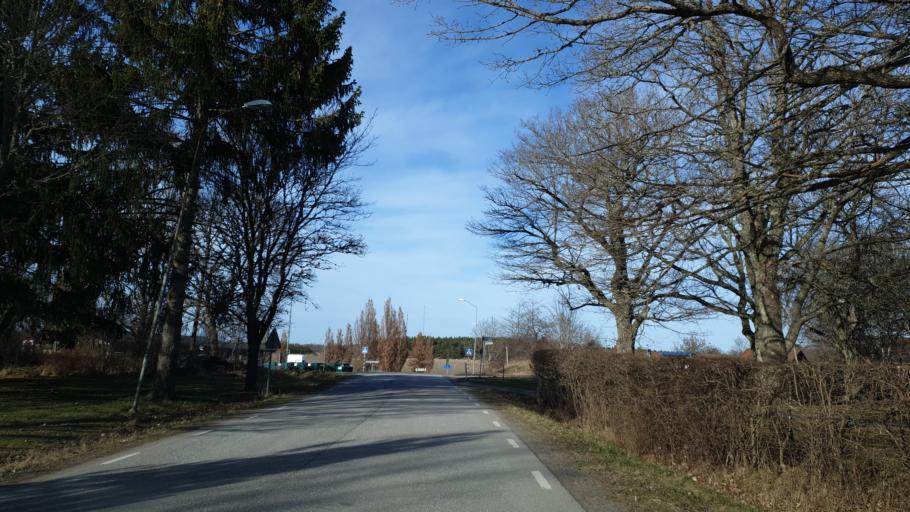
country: SE
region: Uppsala
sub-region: Enkopings Kommun
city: Grillby
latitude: 59.5597
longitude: 17.2464
